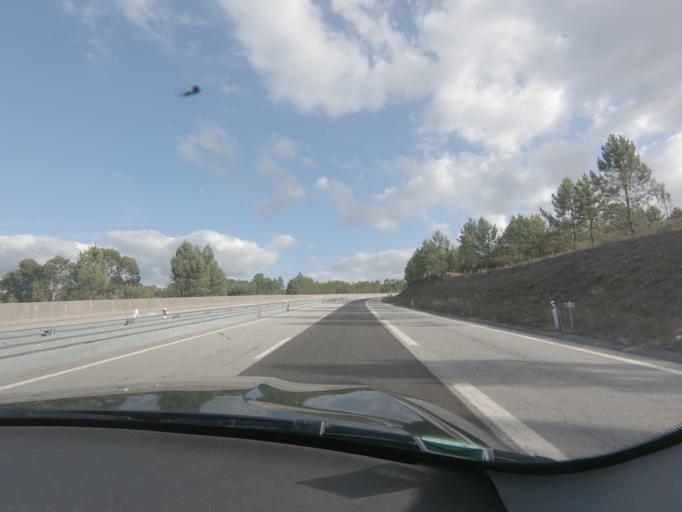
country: PT
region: Viseu
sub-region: Viseu
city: Campo
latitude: 40.7439
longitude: -7.9244
